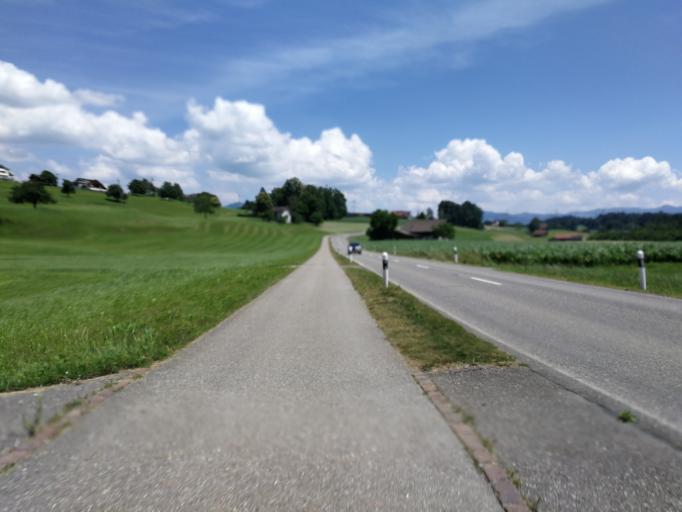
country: CH
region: Saint Gallen
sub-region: Wahlkreis See-Gaster
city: Eschenbach
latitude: 47.2330
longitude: 8.9059
